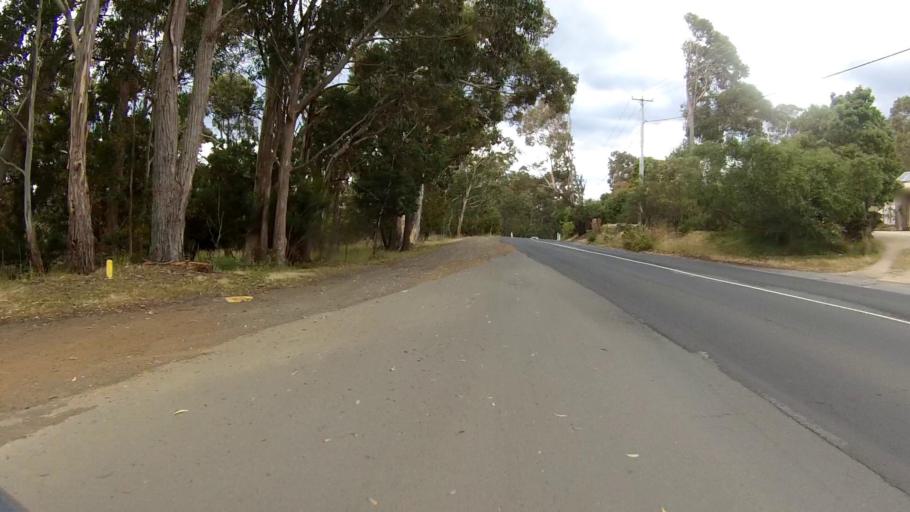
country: AU
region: Tasmania
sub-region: Hobart
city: Dynnyrne
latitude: -42.9052
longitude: 147.2806
